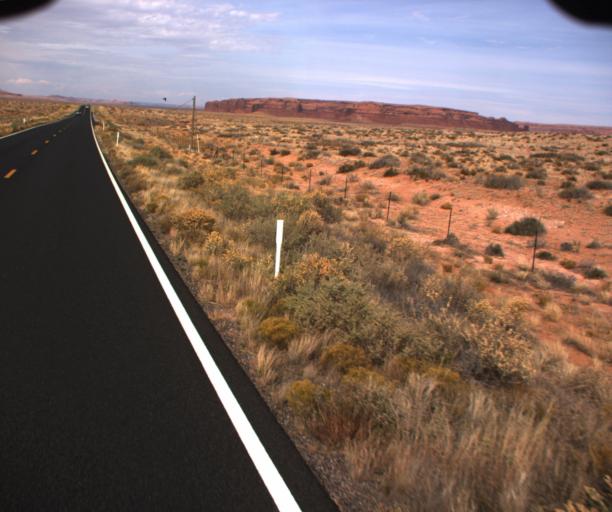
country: US
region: Arizona
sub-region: Apache County
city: Many Farms
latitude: 36.5637
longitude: -109.5423
